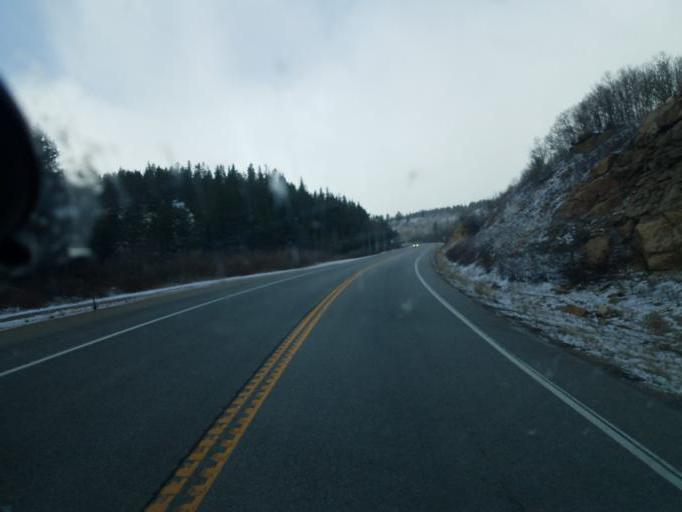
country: US
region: Colorado
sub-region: Clear Creek County
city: Georgetown
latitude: 39.4425
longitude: -105.7442
